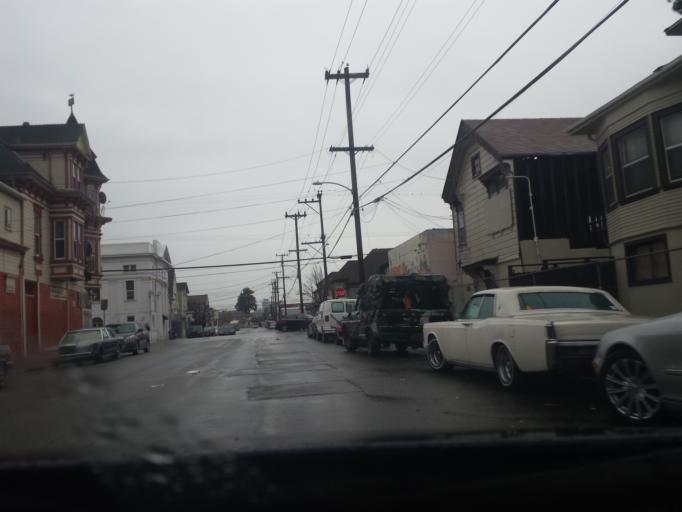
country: US
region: California
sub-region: Alameda County
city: Emeryville
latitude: 37.8256
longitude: -122.2810
